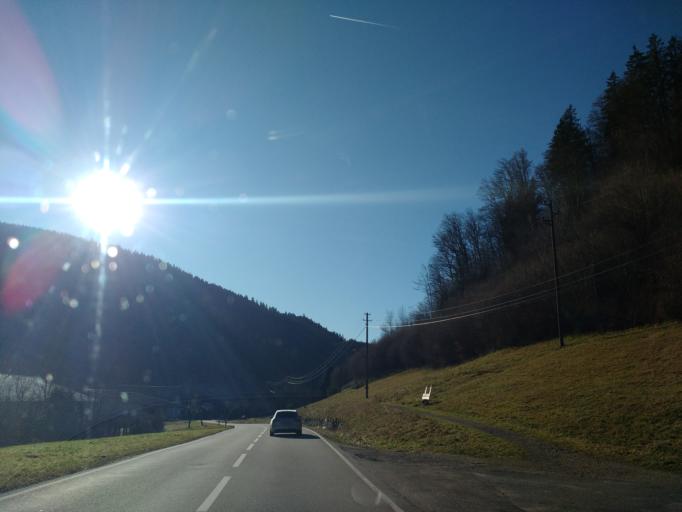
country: DE
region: Baden-Wuerttemberg
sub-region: Karlsruhe Region
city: Bad Rippoldsau-Schapbach
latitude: 48.4159
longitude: 8.3301
